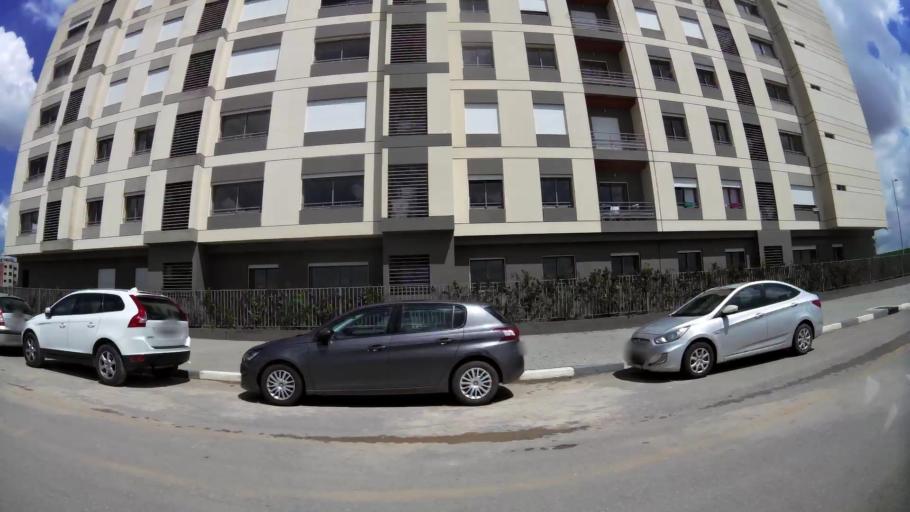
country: MA
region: Chaouia-Ouardigha
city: Nouaseur
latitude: 33.3883
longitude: -7.5603
